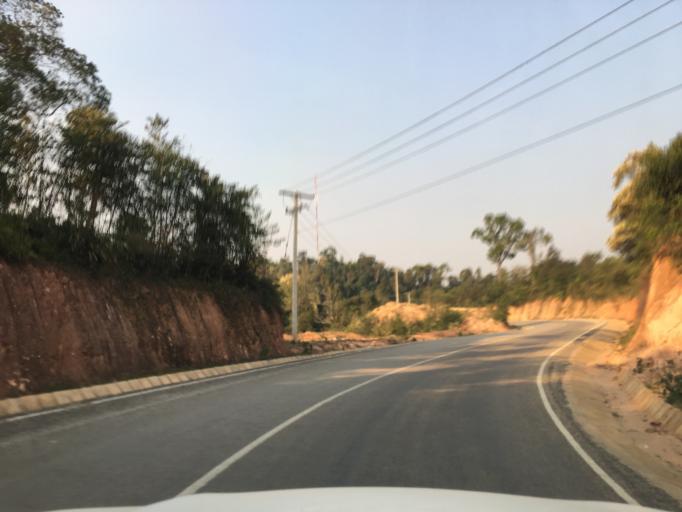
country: LA
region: Houaphan
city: Xam Nua
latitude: 20.6058
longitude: 104.0735
